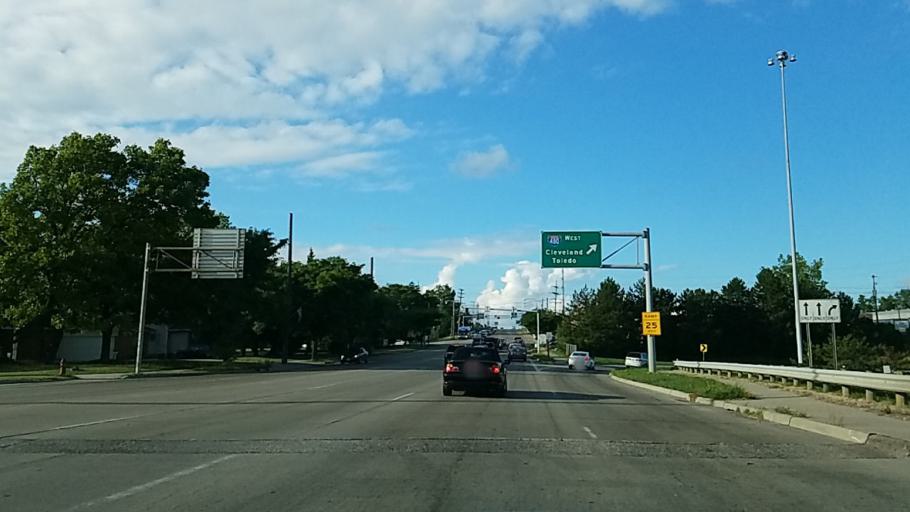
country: US
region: Ohio
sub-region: Cuyahoga County
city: Warrensville Heights
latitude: 41.4251
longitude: -81.5371
